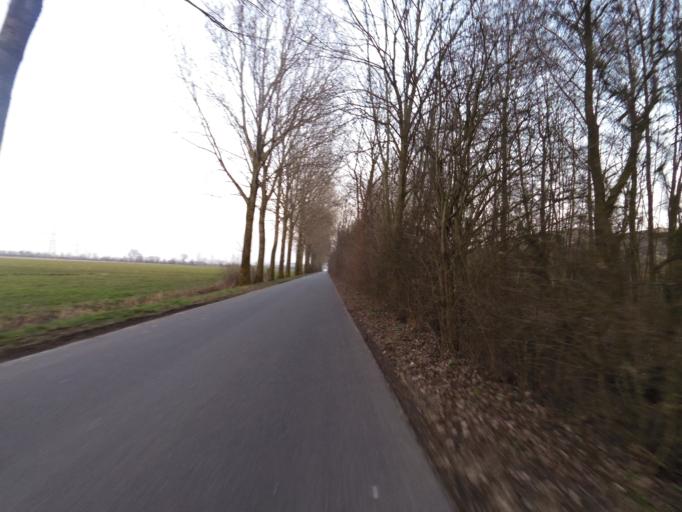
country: NL
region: Gelderland
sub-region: Gemeente Zevenaar
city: Zevenaar
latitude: 51.9548
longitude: 6.0850
